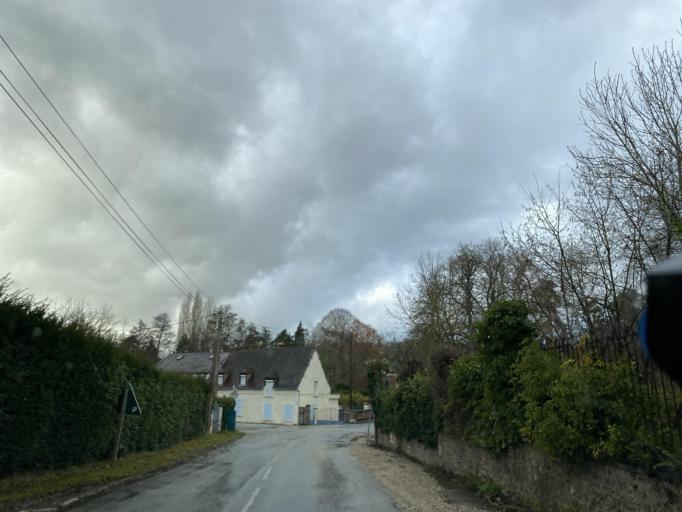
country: FR
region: Haute-Normandie
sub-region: Departement de l'Eure
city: Tillieres-sur-Avre
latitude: 48.7567
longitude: 1.0606
